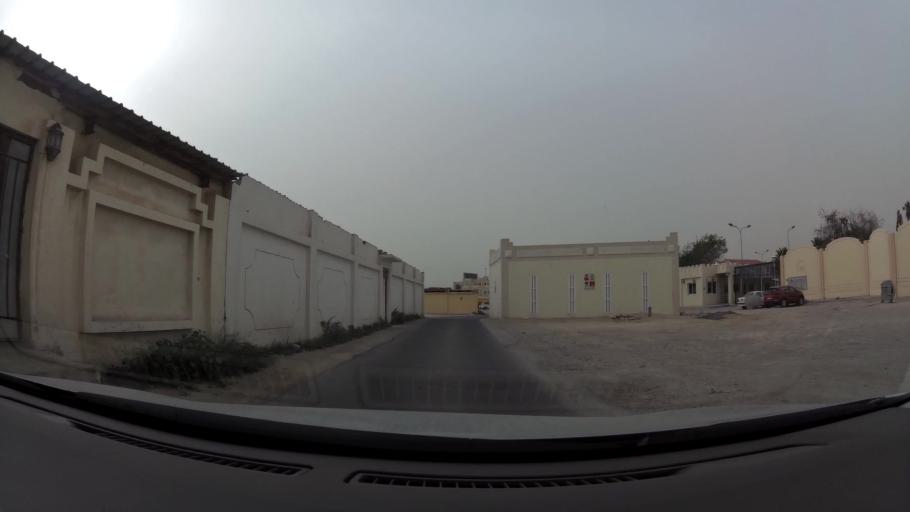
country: QA
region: Baladiyat ad Dawhah
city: Doha
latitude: 25.2553
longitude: 51.4878
